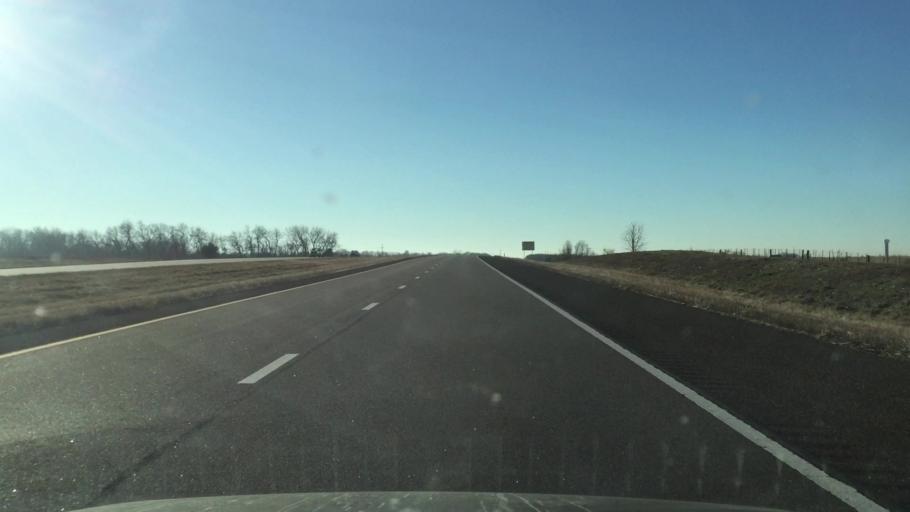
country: US
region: Kansas
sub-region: Miami County
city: Paola
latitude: 38.6120
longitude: -94.8358
